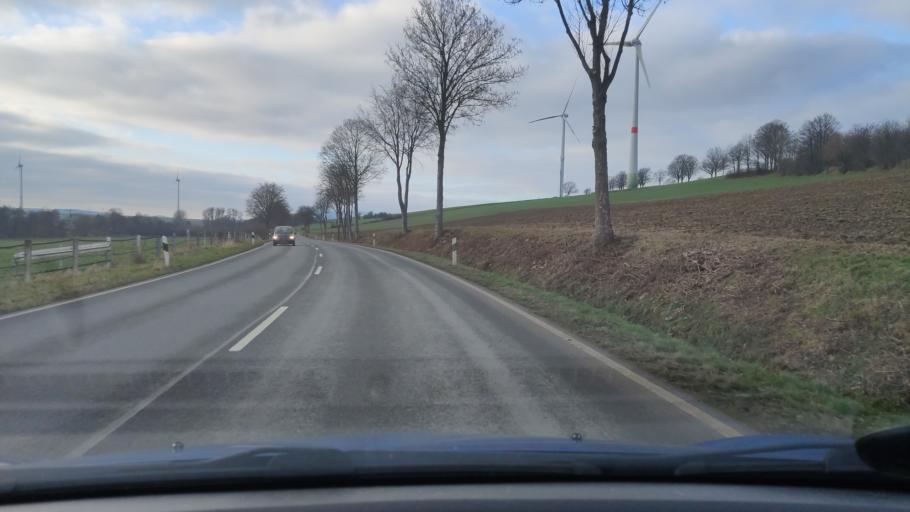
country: DE
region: Lower Saxony
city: Coppenbrugge
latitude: 52.1350
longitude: 9.5373
